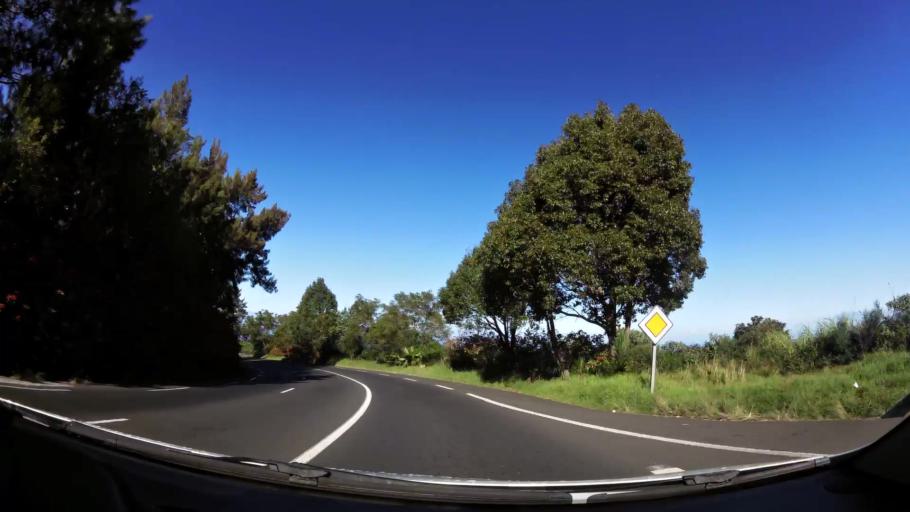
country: RE
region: Reunion
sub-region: Reunion
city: Le Tampon
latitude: -21.2330
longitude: 55.5401
